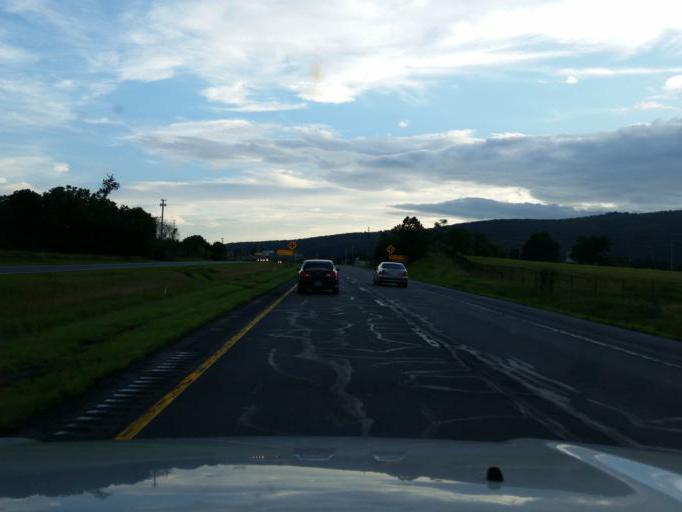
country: US
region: Maryland
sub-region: Frederick County
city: Emmitsburg
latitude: 39.6892
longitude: -77.3296
